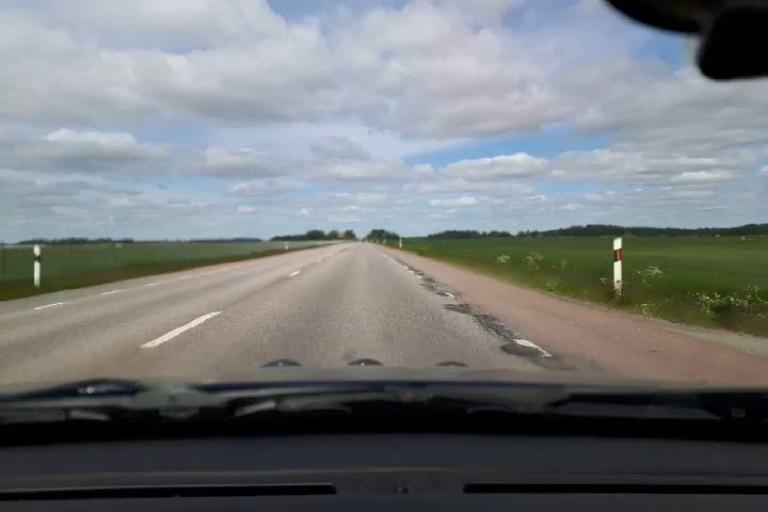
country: SE
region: Uppsala
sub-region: Uppsala Kommun
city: Gamla Uppsala
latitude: 59.8941
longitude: 17.6155
